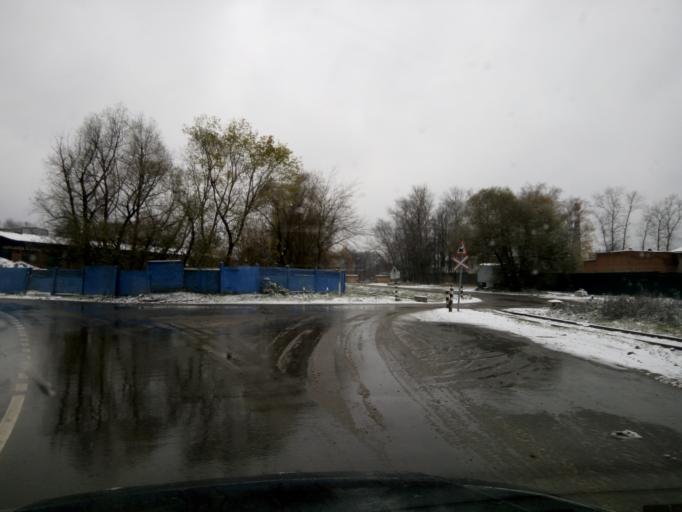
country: RU
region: Moskovskaya
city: Skhodnya
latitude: 55.9483
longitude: 37.2830
